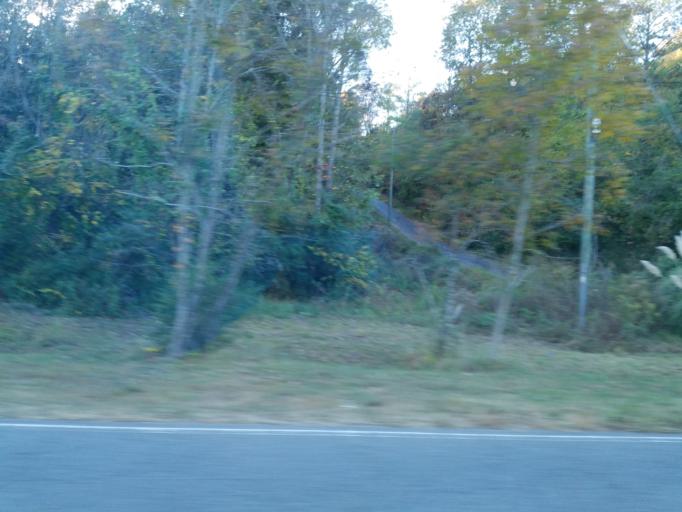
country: US
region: Georgia
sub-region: Bartow County
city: Adairsville
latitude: 34.2904
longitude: -84.9424
